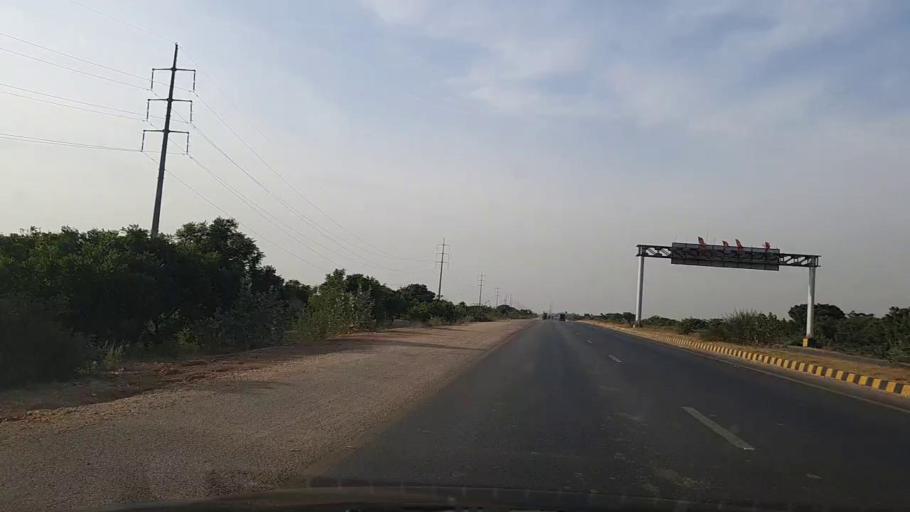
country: PK
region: Sindh
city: Gharo
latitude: 24.7707
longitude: 67.5470
